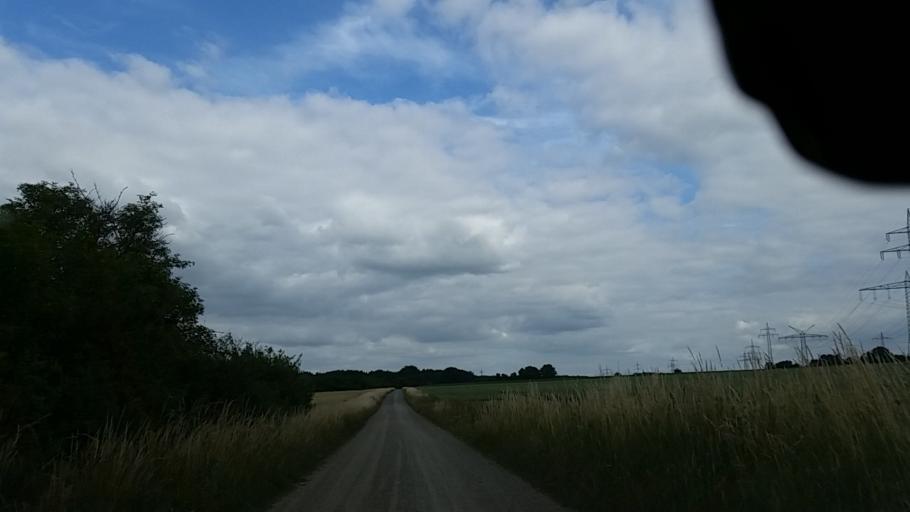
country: DE
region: Lower Saxony
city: Wolfsburg
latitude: 52.3504
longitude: 10.8096
